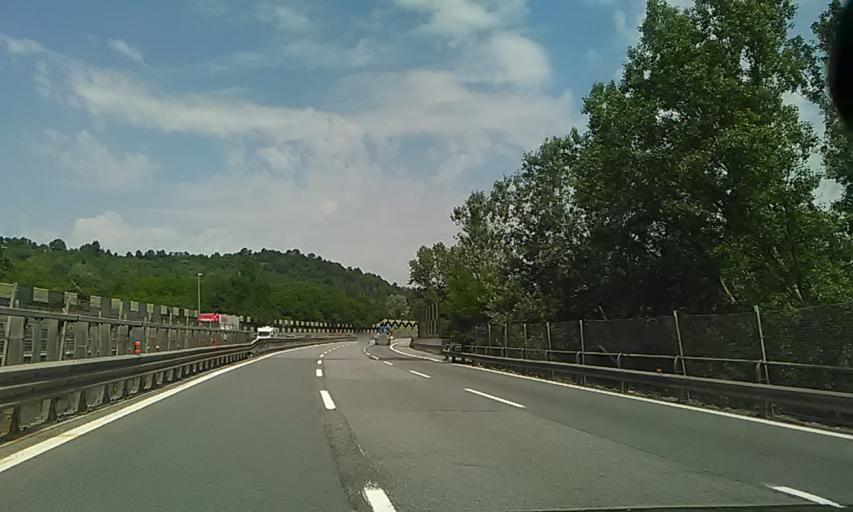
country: IT
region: Piedmont
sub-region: Provincia di Alessandria
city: Rocca Grimalda
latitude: 44.6753
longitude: 8.6583
